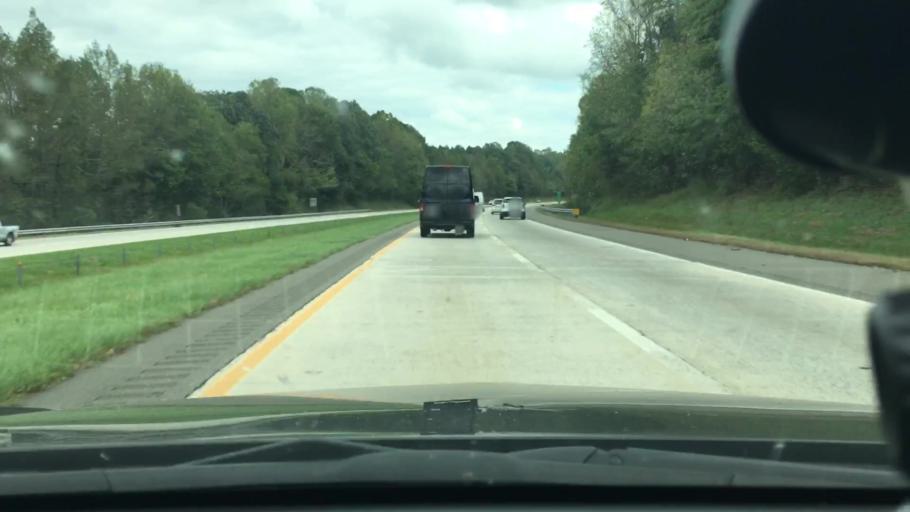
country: US
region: North Carolina
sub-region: Davie County
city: Mocksville
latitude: 35.8677
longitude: -80.7301
